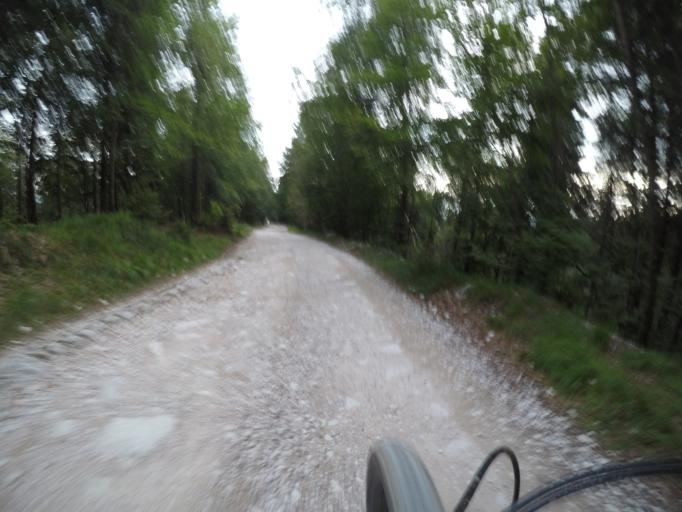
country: IT
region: Veneto
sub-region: Provincia di Vicenza
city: Gallio
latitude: 45.9073
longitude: 11.5245
